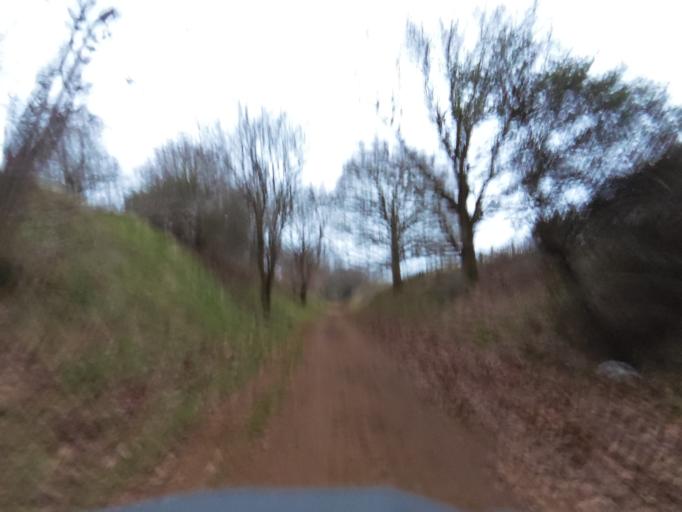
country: GB
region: England
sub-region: Norfolk
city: Costessey
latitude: 52.6955
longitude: 1.2033
